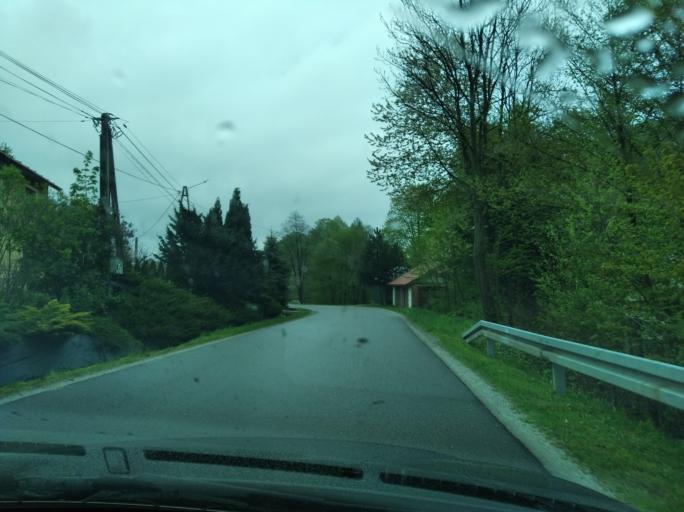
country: PL
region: Subcarpathian Voivodeship
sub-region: Powiat rzeszowski
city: Lecka
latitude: 49.8750
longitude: 21.9970
